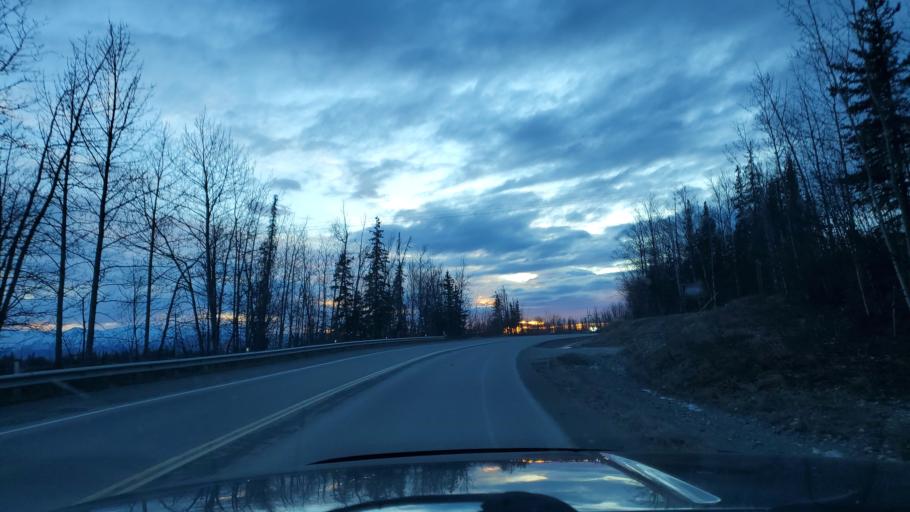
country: US
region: Alaska
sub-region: Matanuska-Susitna Borough
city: Lakes
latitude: 61.6099
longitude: -149.3311
